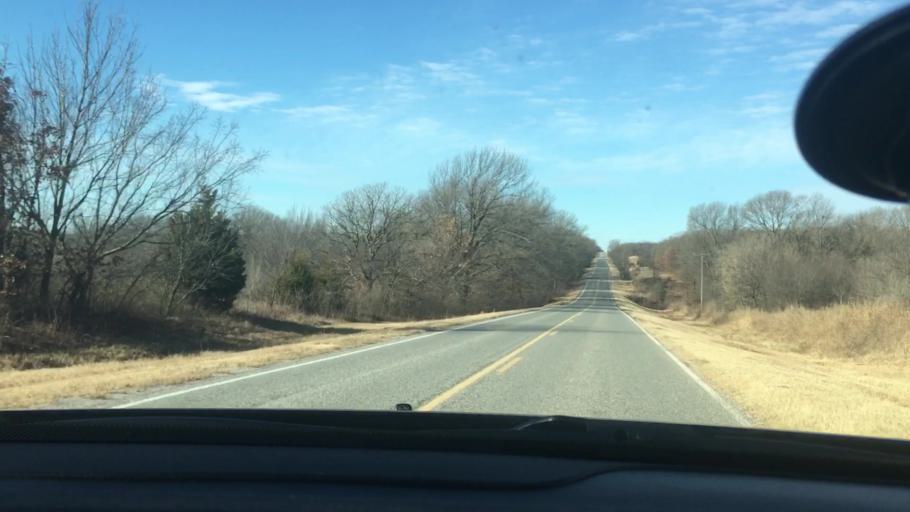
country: US
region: Oklahoma
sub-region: Seminole County
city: Konawa
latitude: 34.9857
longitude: -96.8623
